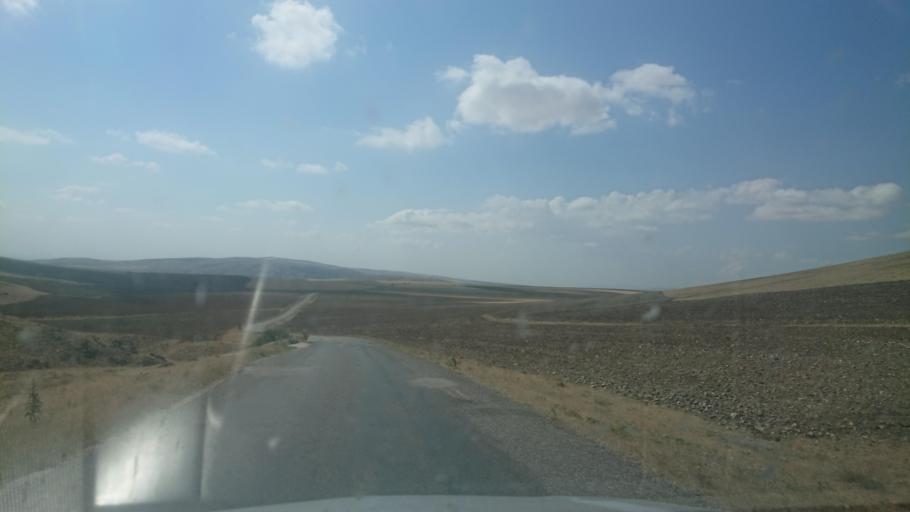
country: TR
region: Aksaray
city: Sariyahsi
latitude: 39.0004
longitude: 33.9750
